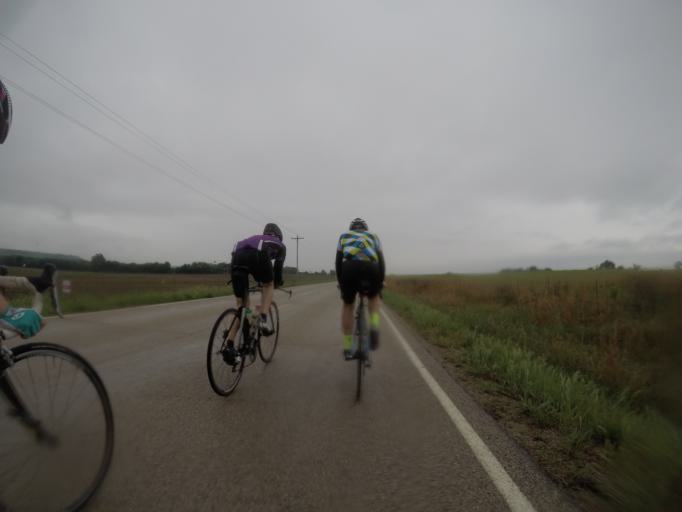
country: US
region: Kansas
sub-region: Pottawatomie County
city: Wamego
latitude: 39.3578
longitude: -96.2214
